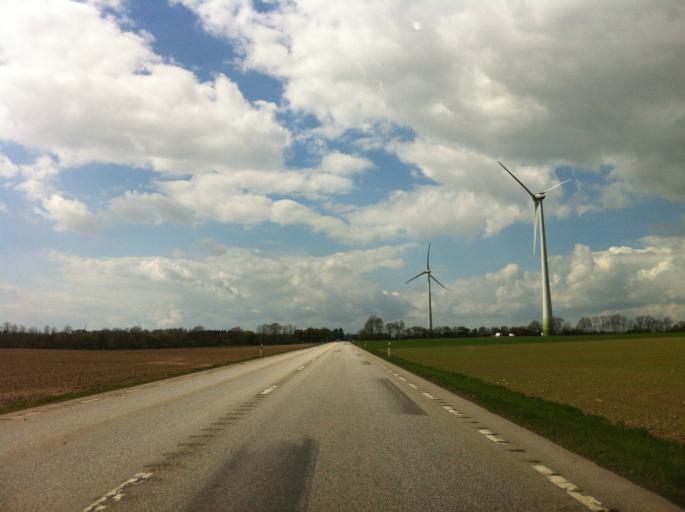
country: SE
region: Skane
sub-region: Hoors Kommun
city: Loberod
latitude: 55.8413
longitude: 13.4911
